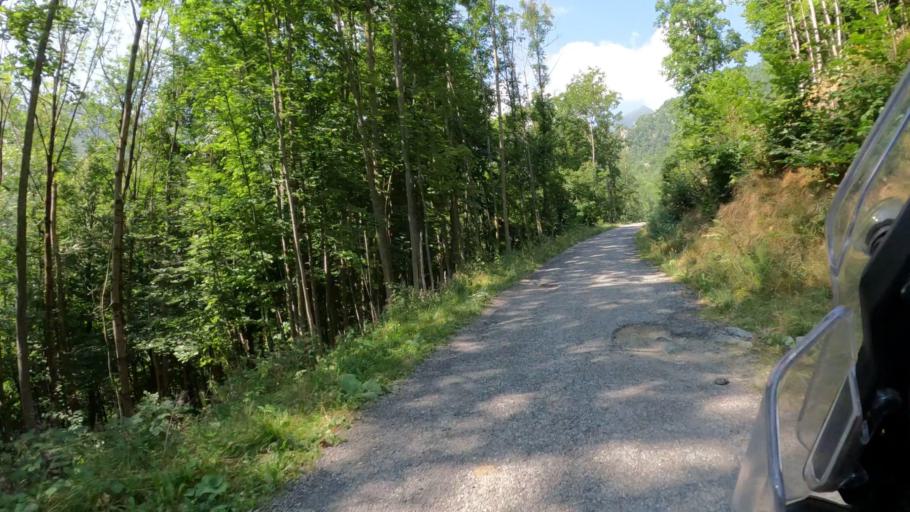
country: IT
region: Piedmont
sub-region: Provincia di Torino
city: Lemie
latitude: 45.2097
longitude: 7.3093
